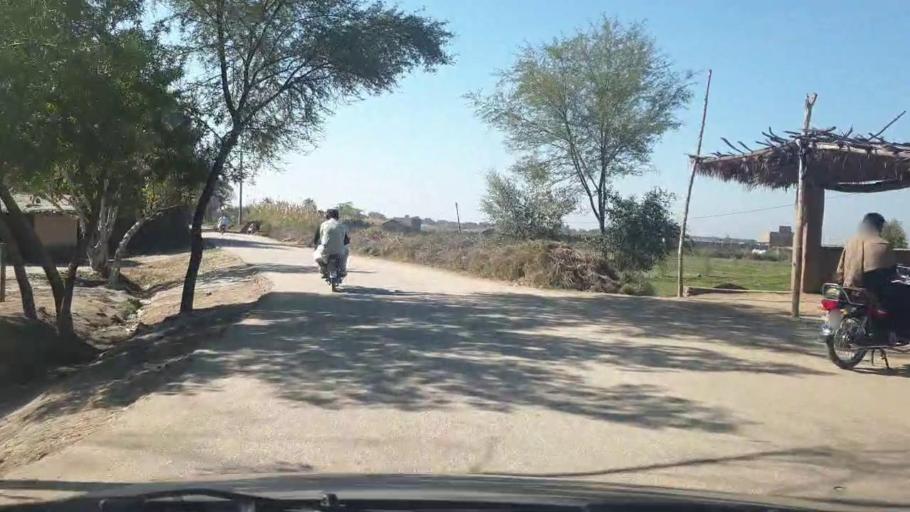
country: PK
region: Sindh
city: Bozdar
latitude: 27.1364
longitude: 68.6440
